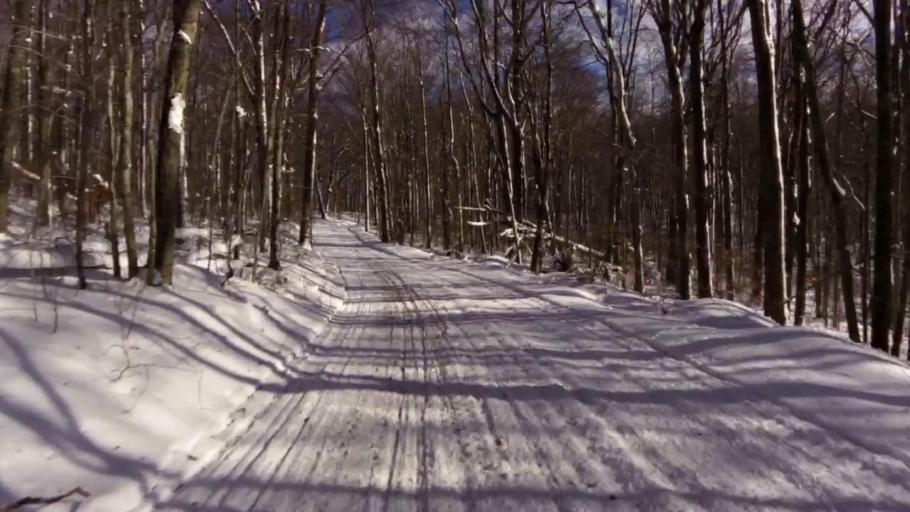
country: US
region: New York
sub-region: Cattaraugus County
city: Salamanca
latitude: 42.0701
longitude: -78.6763
